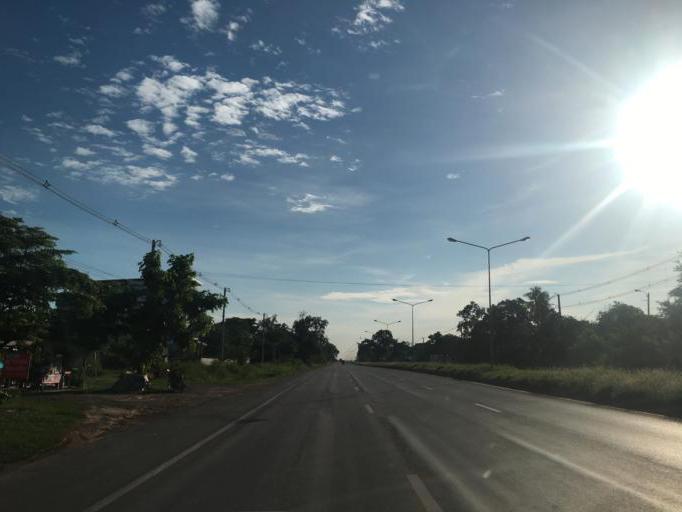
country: TH
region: Changwat Udon Thani
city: Kut Chap
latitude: 17.3255
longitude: 102.6510
